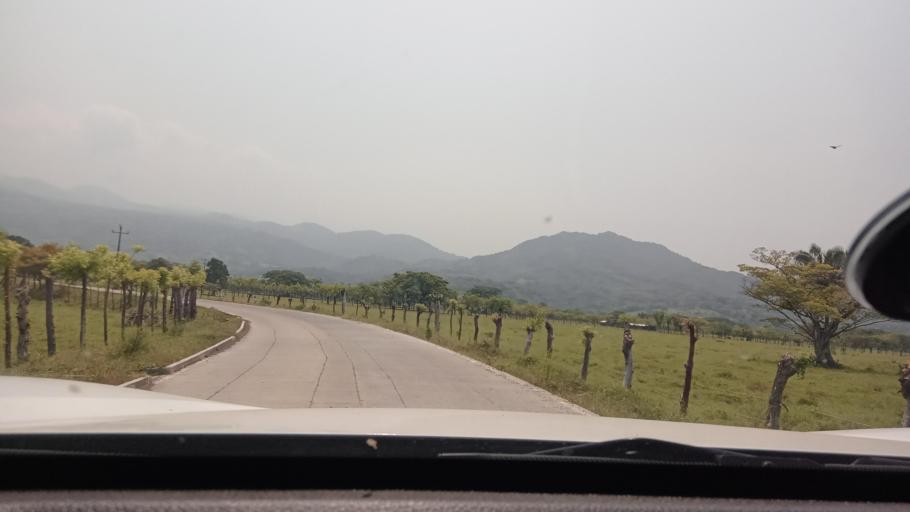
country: MX
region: Veracruz
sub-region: San Andres Tuxtla
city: Santa Rosa Abata
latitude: 18.5635
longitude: -95.0501
